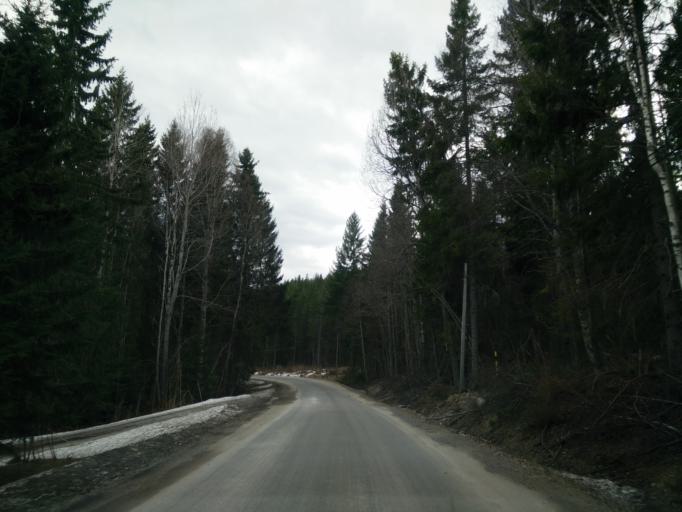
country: SE
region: Vaesternorrland
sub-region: Haernoesands Kommun
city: Haernoesand
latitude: 62.7258
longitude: 18.1003
